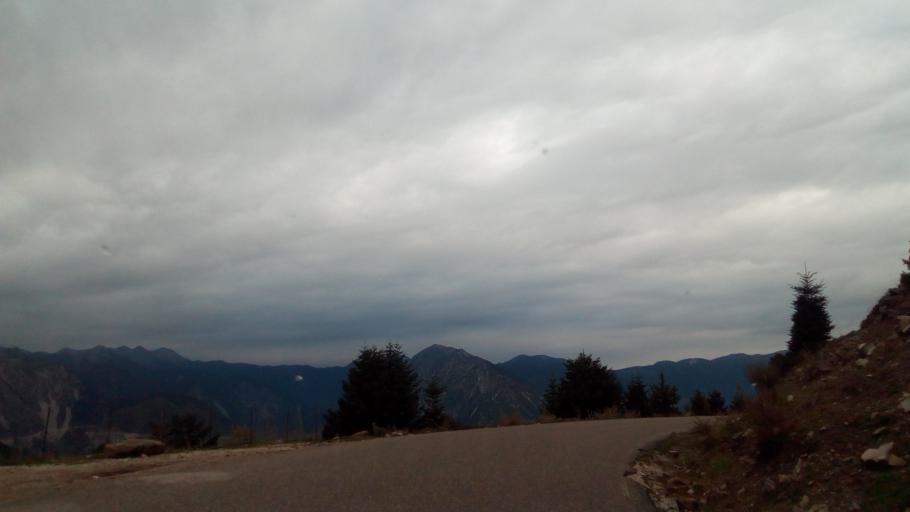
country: GR
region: West Greece
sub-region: Nomos Aitolias kai Akarnanias
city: Thermo
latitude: 38.6286
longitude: 21.8295
